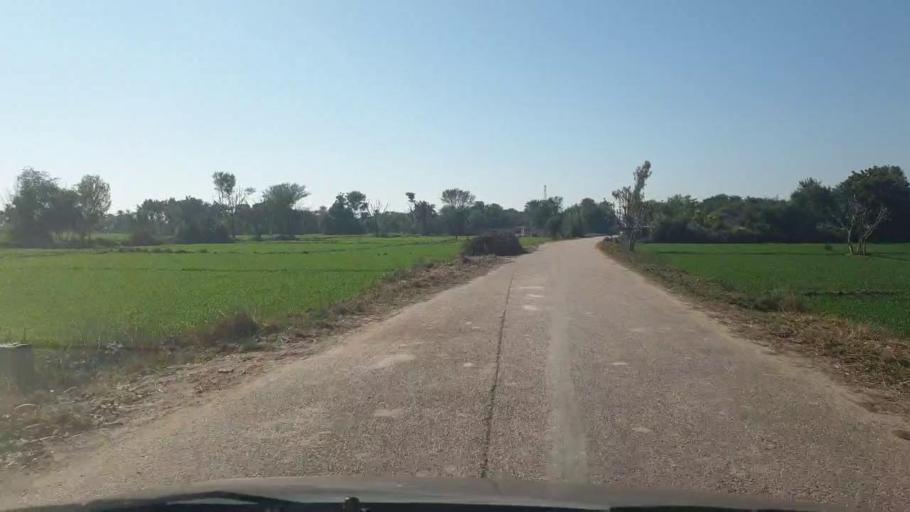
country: PK
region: Sindh
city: Bozdar
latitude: 27.1510
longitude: 68.6530
